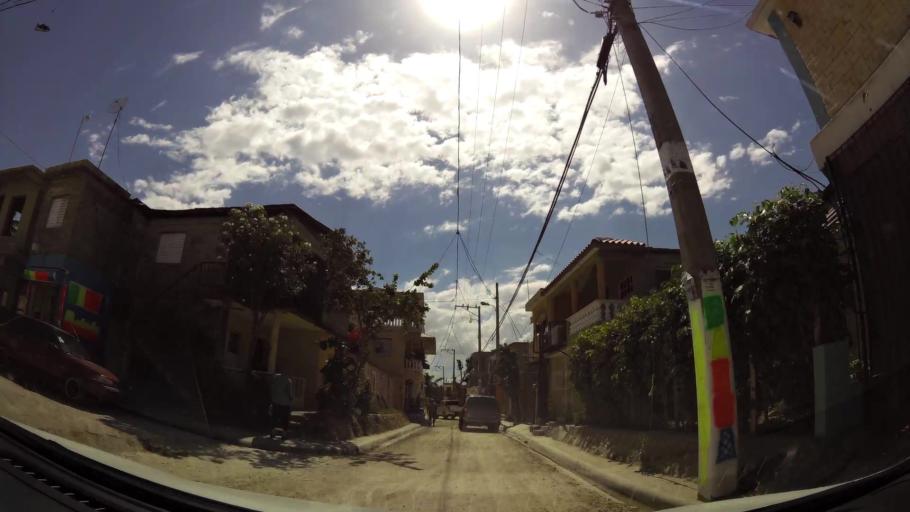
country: DO
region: San Cristobal
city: San Cristobal
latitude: 18.4242
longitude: -70.1045
